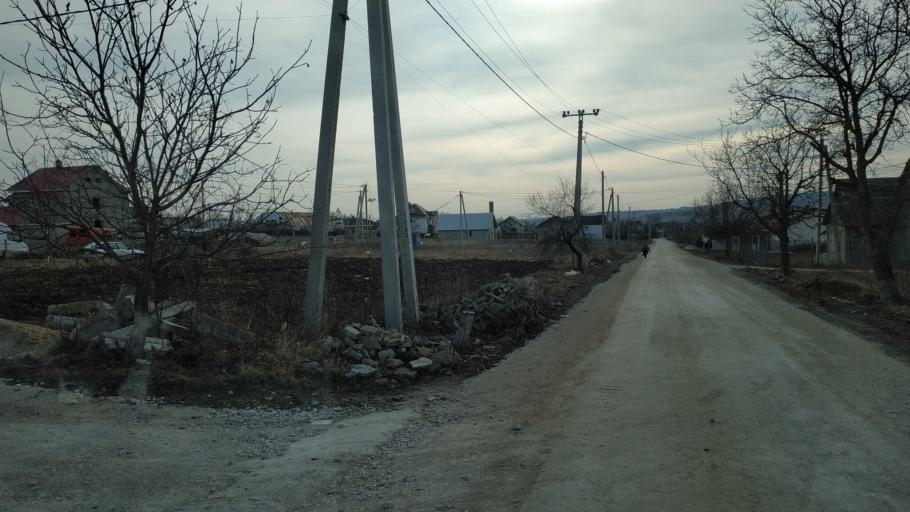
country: MD
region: Chisinau
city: Vatra
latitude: 46.9895
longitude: 28.6686
